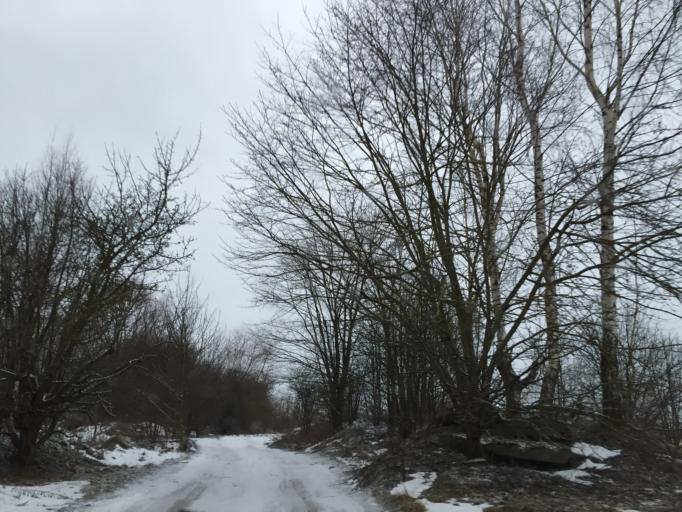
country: LV
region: Riga
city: Riga
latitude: 56.9211
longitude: 24.1325
